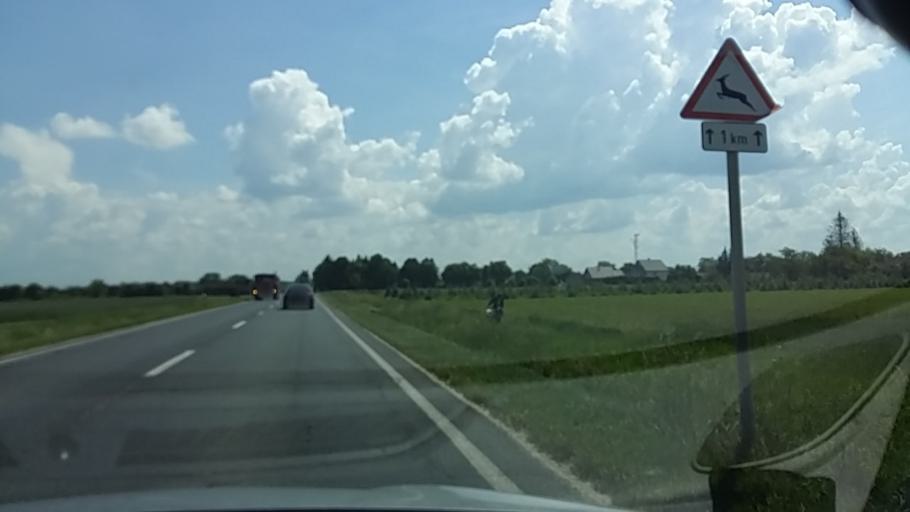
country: AT
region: Burgenland
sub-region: Politischer Bezirk Gussing
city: Heiligenbrunn
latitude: 46.9672
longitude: 16.4509
